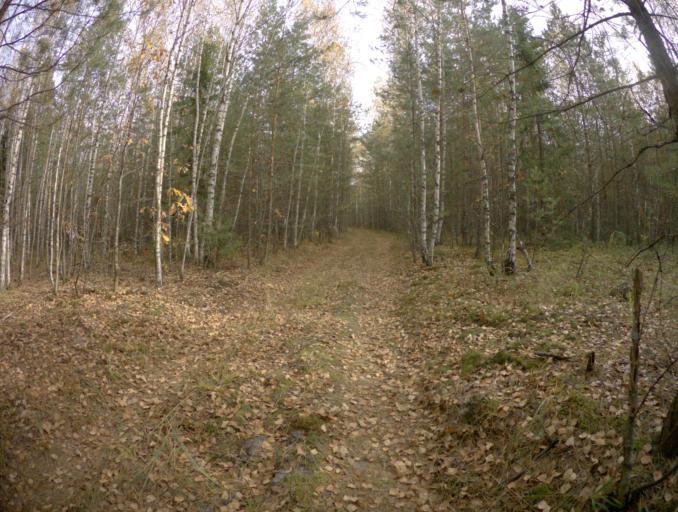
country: RU
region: Vladimir
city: Vorsha
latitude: 55.9660
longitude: 40.1427
